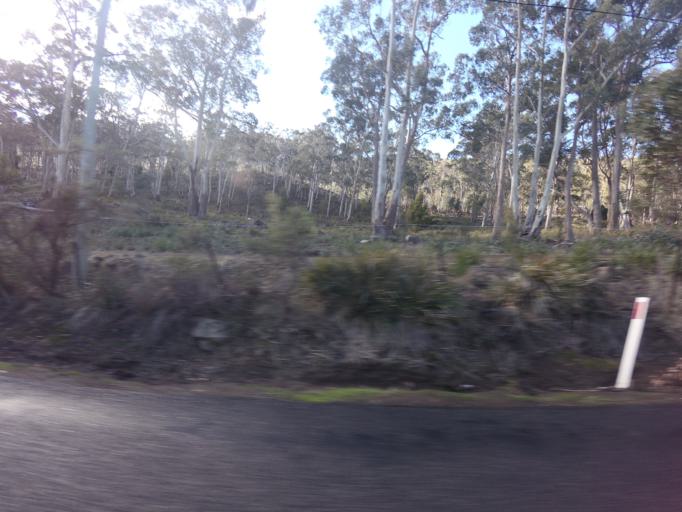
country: AU
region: Tasmania
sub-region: Glenorchy
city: Berriedale
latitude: -42.8157
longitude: 147.1758
